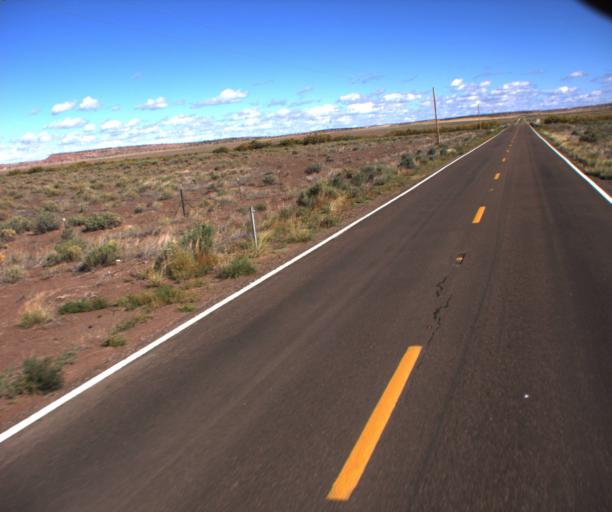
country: US
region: Arizona
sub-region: Apache County
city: Saint Johns
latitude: 34.6126
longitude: -109.3194
